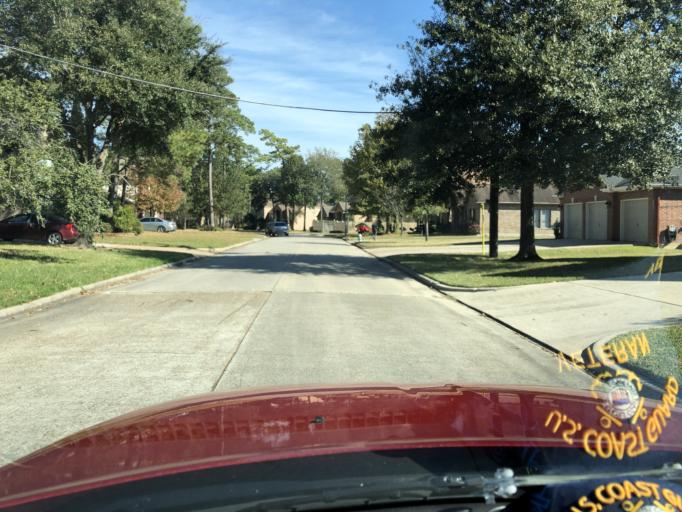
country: US
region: Texas
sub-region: Harris County
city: Tomball
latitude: 30.0185
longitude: -95.5551
